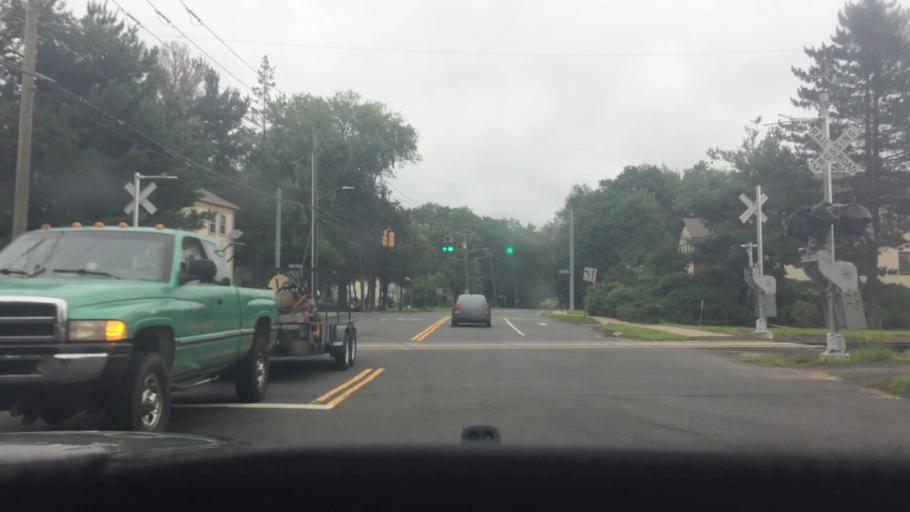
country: US
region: Connecticut
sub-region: Hartford County
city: Blue Hills
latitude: 41.8325
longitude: -72.7342
